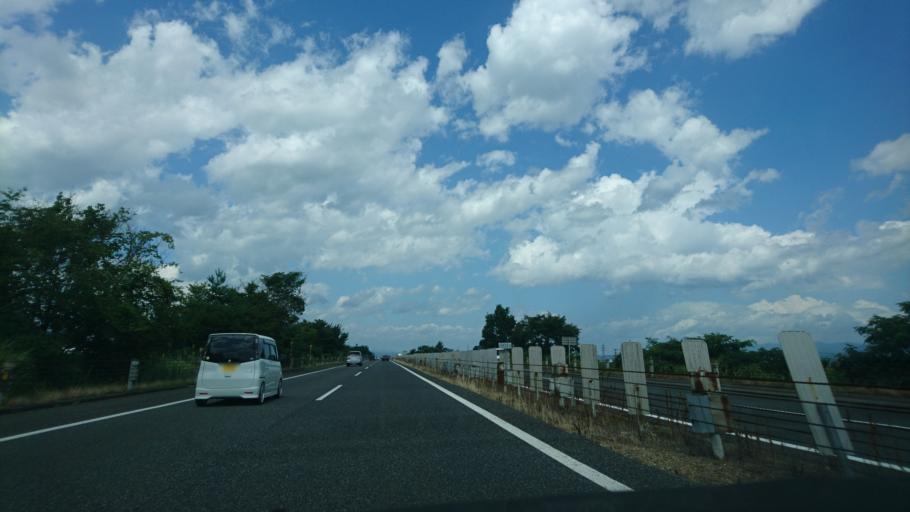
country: JP
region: Iwate
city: Morioka-shi
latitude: 39.6360
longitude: 141.1267
